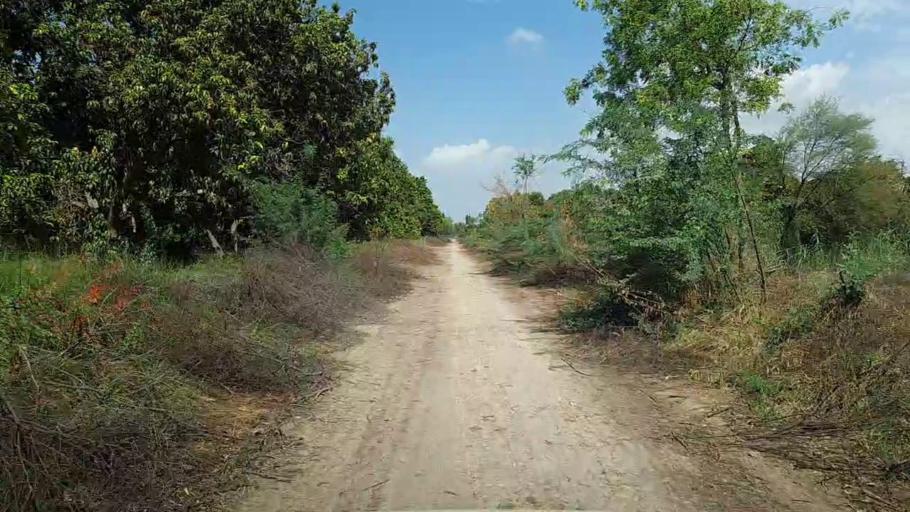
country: PK
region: Sindh
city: Bhiria
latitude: 26.9213
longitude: 68.2191
